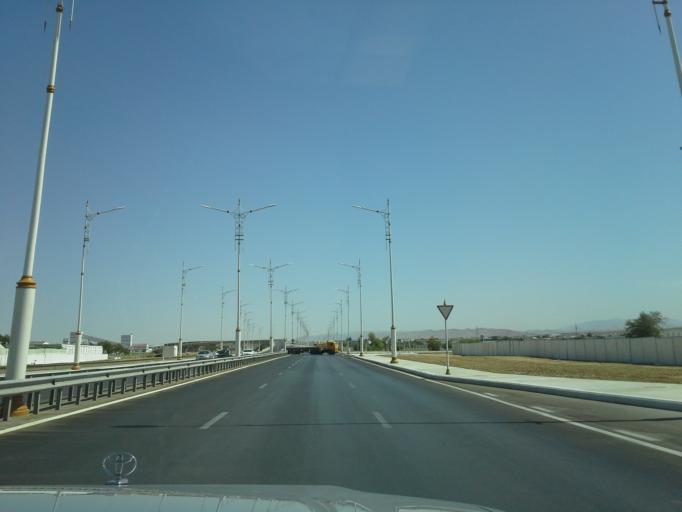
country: TM
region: Ahal
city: Ashgabat
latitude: 37.9323
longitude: 58.4159
